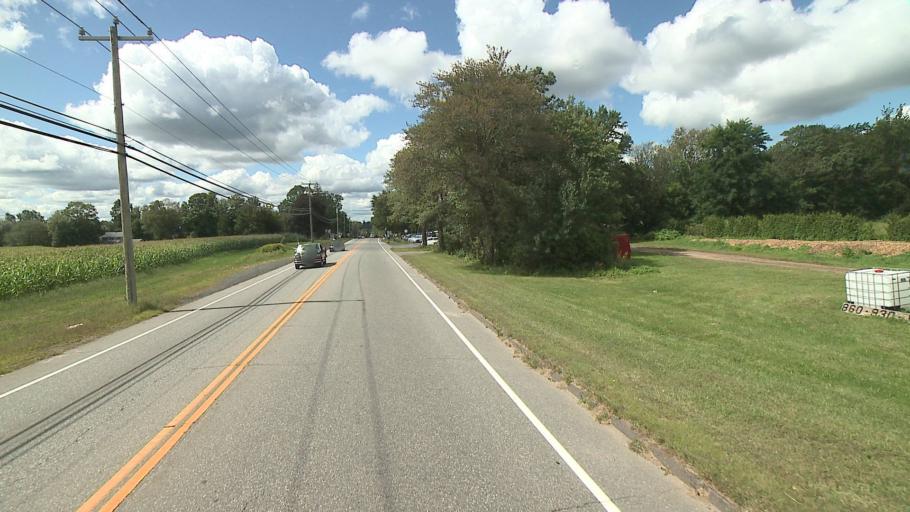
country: US
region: Connecticut
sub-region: Tolland County
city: Coventry Lake
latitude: 41.7982
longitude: -72.3895
